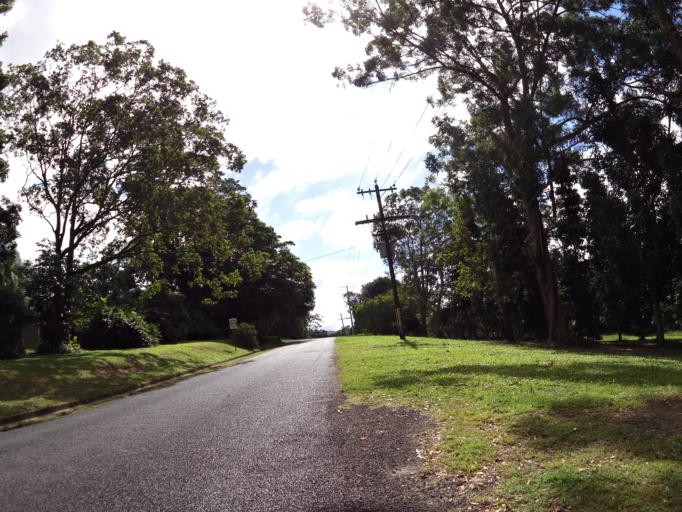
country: AU
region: Queensland
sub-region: Tablelands
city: Kuranda
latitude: -16.8208
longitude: 145.6395
